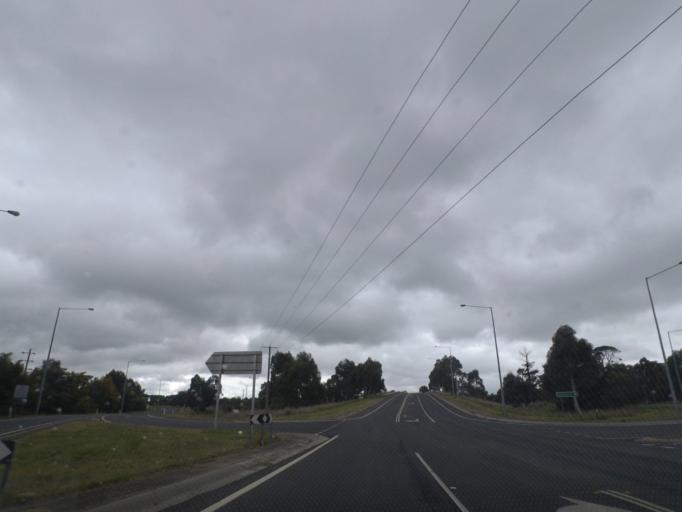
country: AU
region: Victoria
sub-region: Hume
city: Sunbury
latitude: -37.3226
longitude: 144.5243
